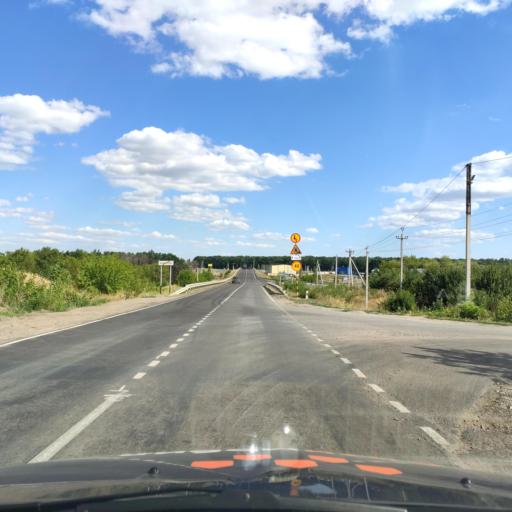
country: RU
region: Voronezj
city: Somovo
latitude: 51.6966
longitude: 39.3801
